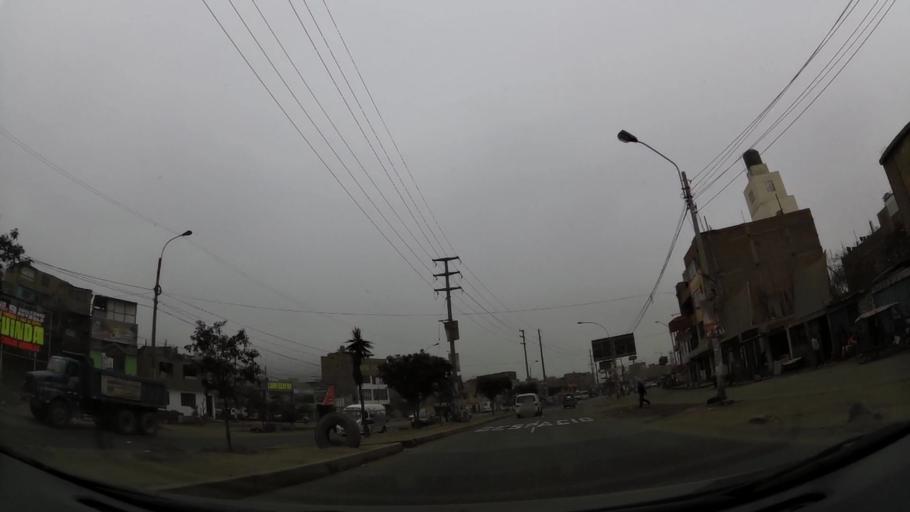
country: PE
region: Lima
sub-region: Lima
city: Urb. Santo Domingo
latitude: -11.8866
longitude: -77.0234
